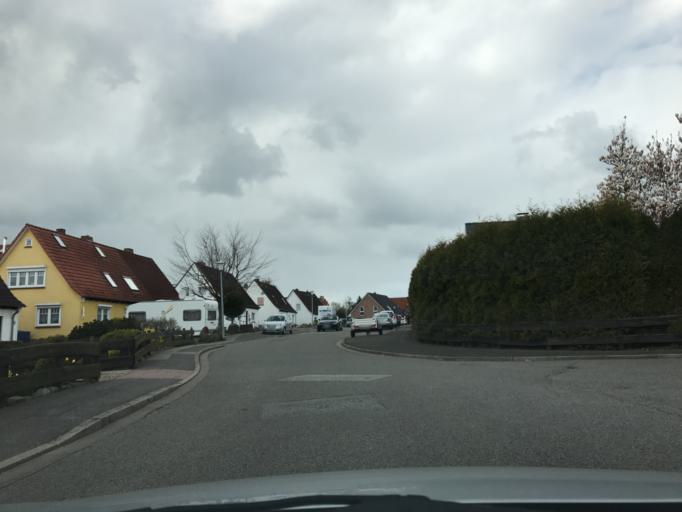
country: DE
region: Schleswig-Holstein
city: Neustadt in Holstein
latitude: 54.0954
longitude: 10.8250
